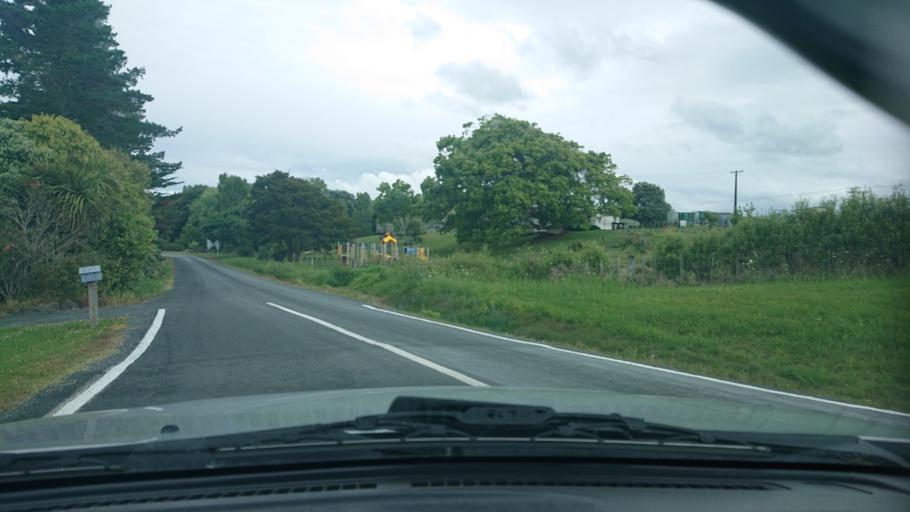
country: NZ
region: Auckland
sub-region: Auckland
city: Wellsford
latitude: -36.3774
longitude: 174.4524
